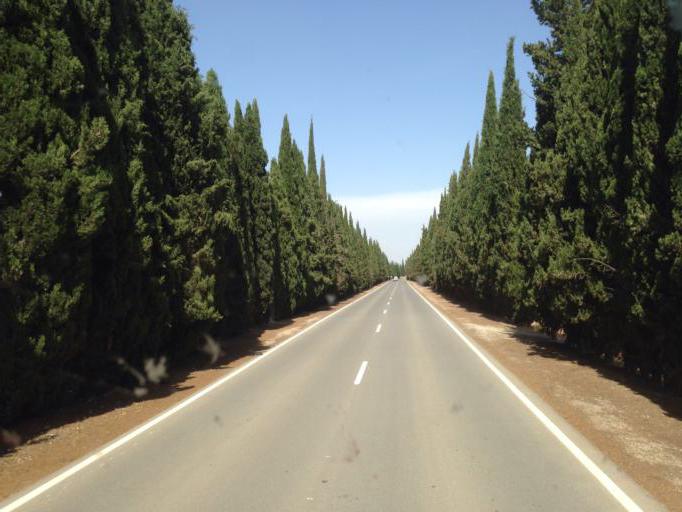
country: ES
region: Andalusia
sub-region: Provincia de Malaga
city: Antequera
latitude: 37.0569
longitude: -4.5857
